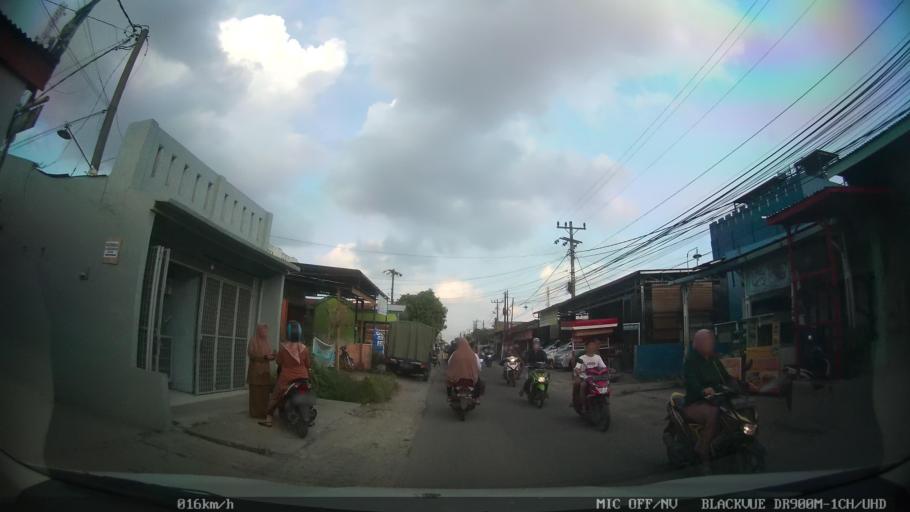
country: ID
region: North Sumatra
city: Medan
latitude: 3.5853
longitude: 98.7391
